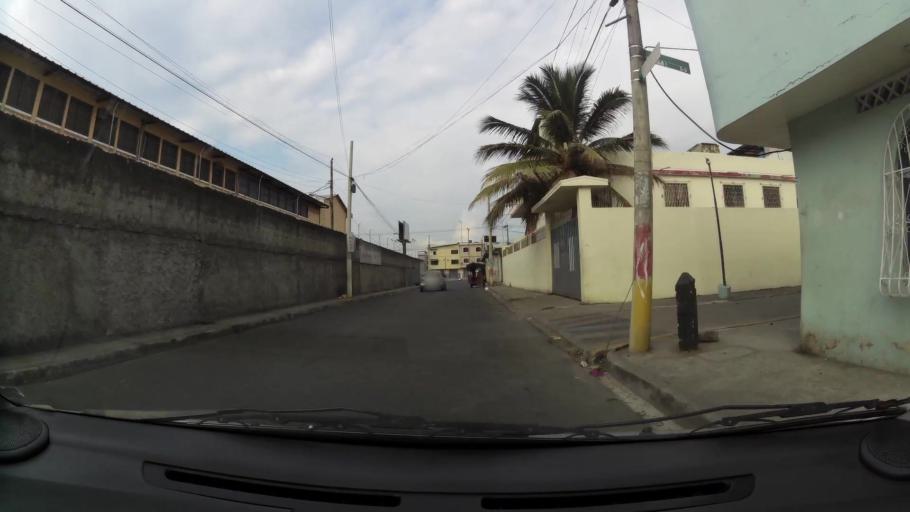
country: EC
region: Guayas
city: Guayaquil
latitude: -2.2491
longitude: -79.8957
